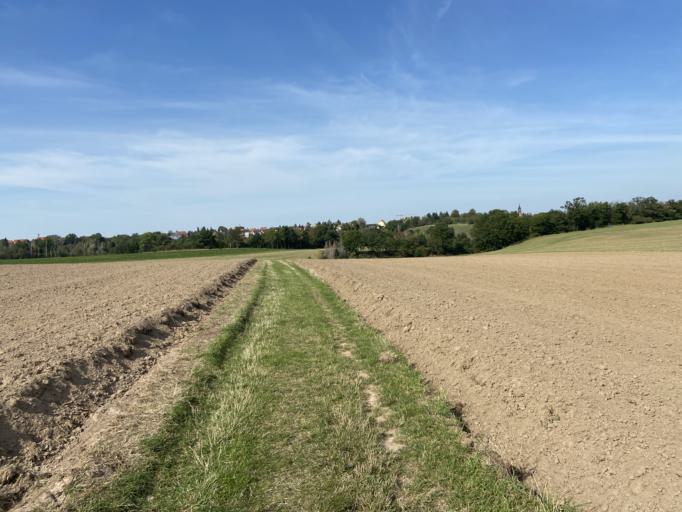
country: DE
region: Saxony
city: Tharandt
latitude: 51.0234
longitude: 13.5928
